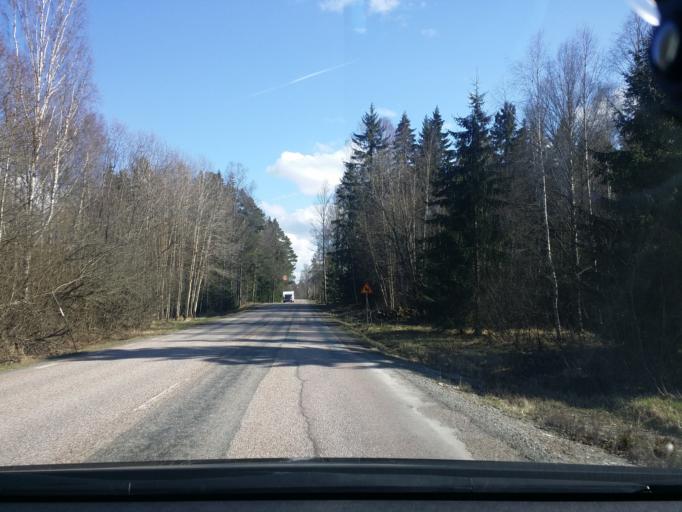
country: SE
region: Vaestmanland
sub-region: Sala Kommun
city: Sala
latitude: 59.9757
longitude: 16.4959
